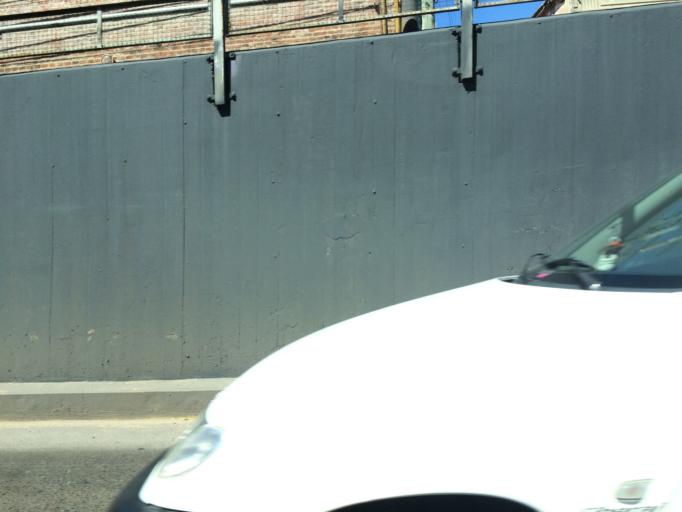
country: AR
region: Buenos Aires
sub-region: Partido de Lomas de Zamora
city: Lomas de Zamora
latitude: -34.7359
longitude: -58.3937
